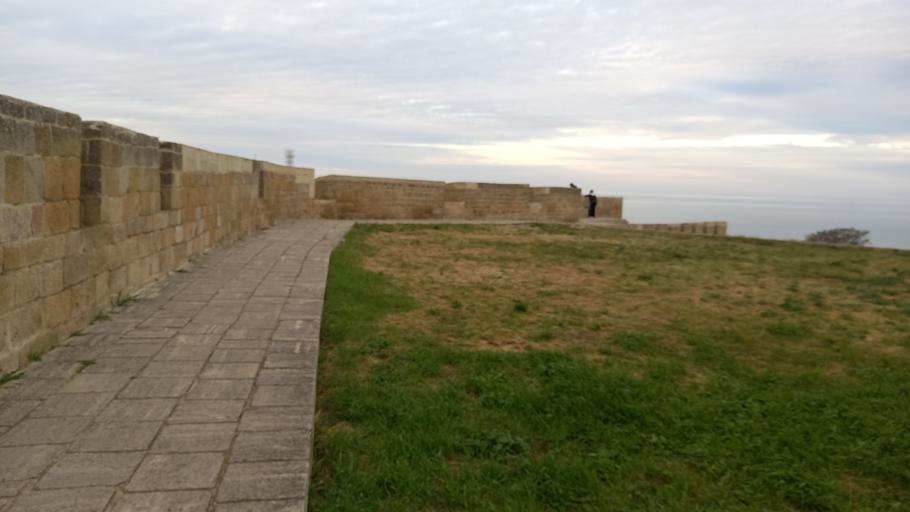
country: RU
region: Dagestan
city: Derbent
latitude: 42.0535
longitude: 48.2734
